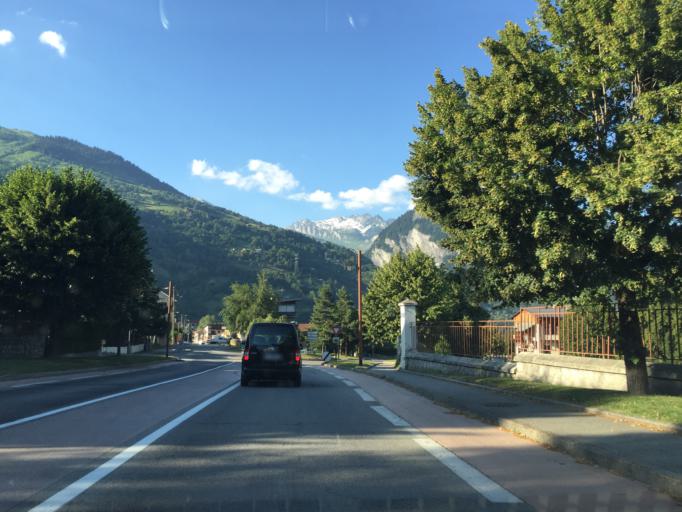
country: FR
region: Rhone-Alpes
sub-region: Departement de la Savoie
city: Bourg-Saint-Maurice
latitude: 45.6132
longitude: 6.7659
